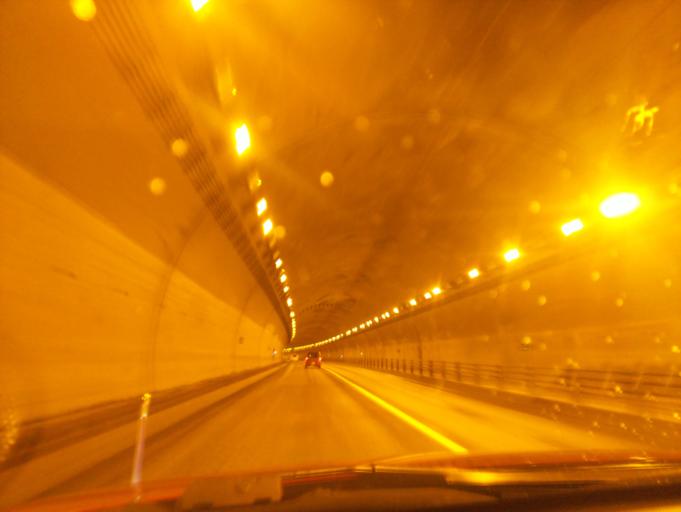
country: JP
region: Hokkaido
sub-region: Asahikawa-shi
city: Asahikawa
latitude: 43.8472
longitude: 142.4523
